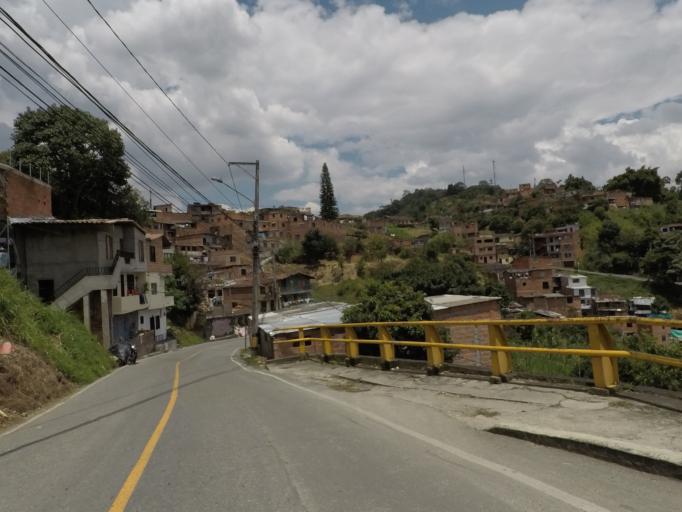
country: CO
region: Antioquia
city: Medellin
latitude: 6.2695
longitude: -75.6294
